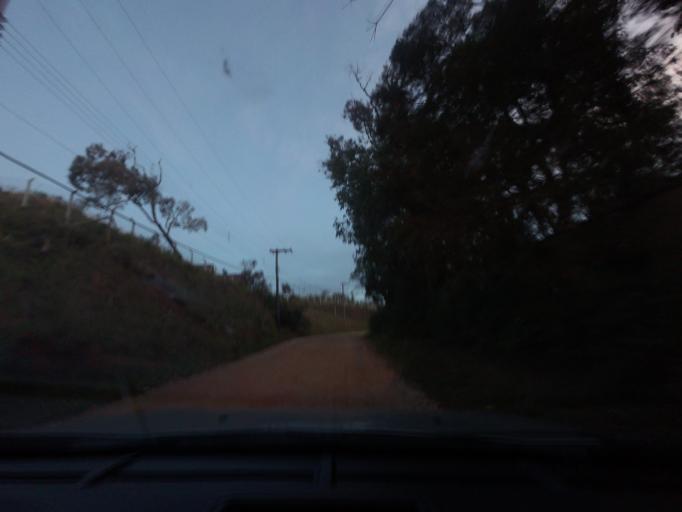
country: BR
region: Sao Paulo
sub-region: Campos Do Jordao
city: Campos do Jordao
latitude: -22.7379
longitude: -45.5461
